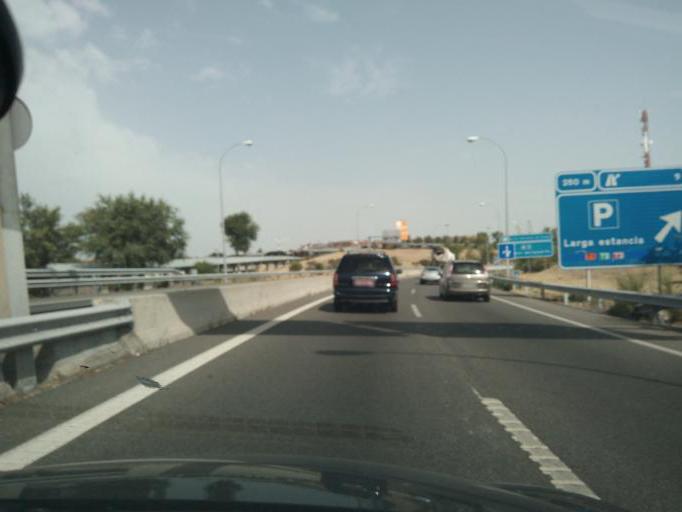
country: ES
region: Madrid
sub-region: Provincia de Madrid
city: Barajas de Madrid
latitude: 40.4631
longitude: -3.5796
